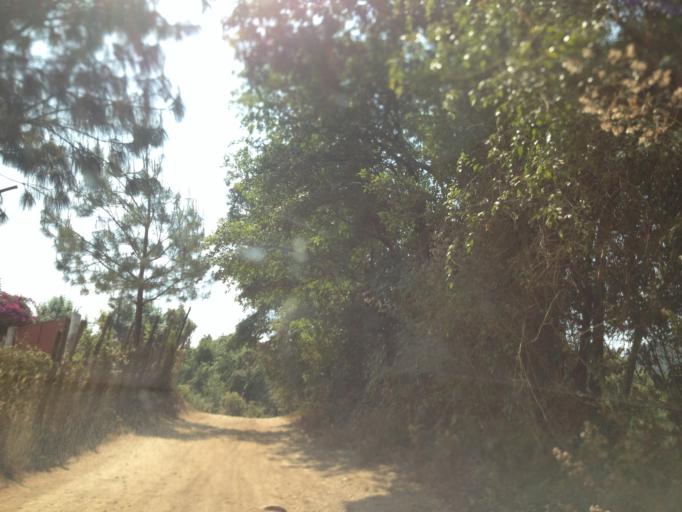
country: MX
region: Michoacan
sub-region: Zitacuaro
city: Macutzio
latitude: 19.4938
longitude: -100.3248
